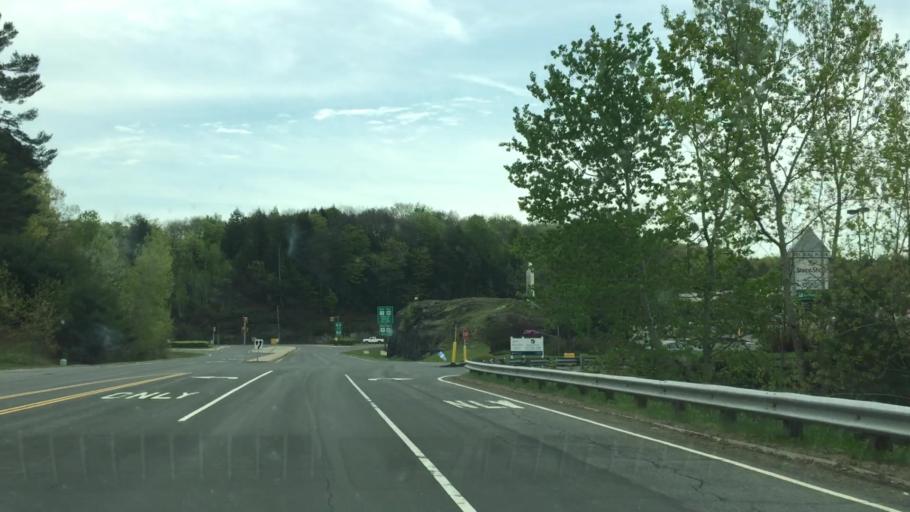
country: US
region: Massachusetts
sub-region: Berkshire County
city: Pittsfield
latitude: 42.4110
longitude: -73.2653
